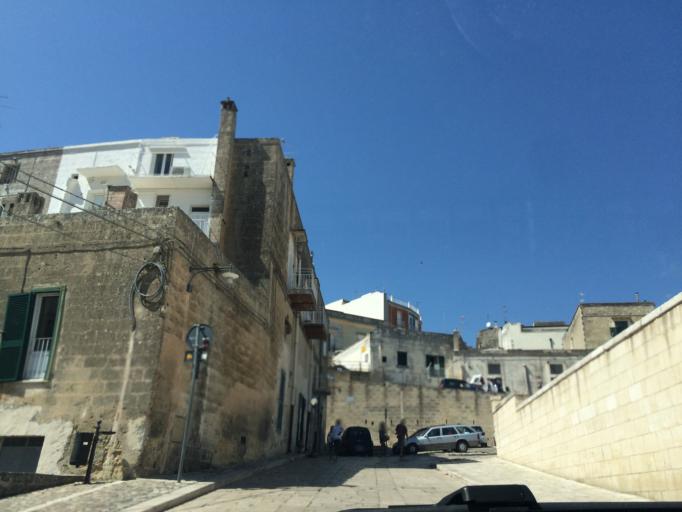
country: IT
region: Basilicate
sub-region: Provincia di Matera
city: Matera
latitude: 40.6701
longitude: 16.6096
